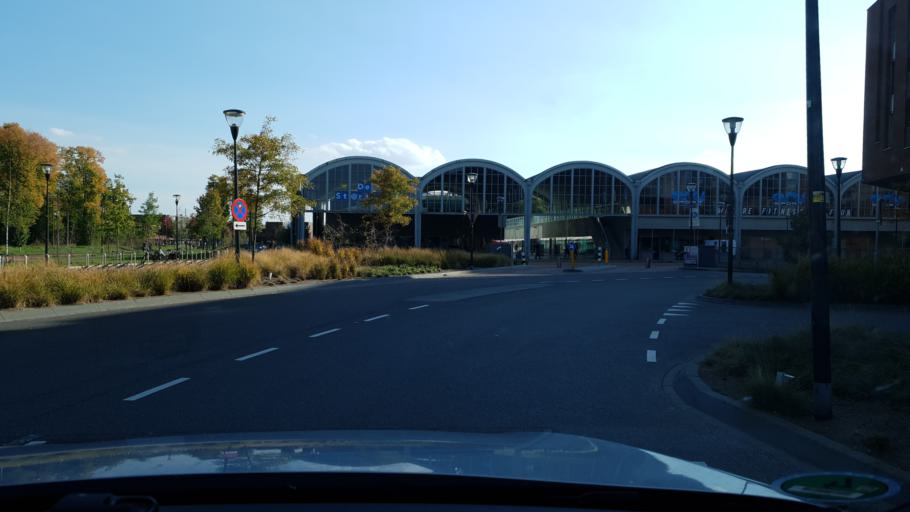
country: NL
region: North Brabant
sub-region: Gemeente Eindhoven
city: Meerhoven
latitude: 51.4437
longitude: 5.4109
